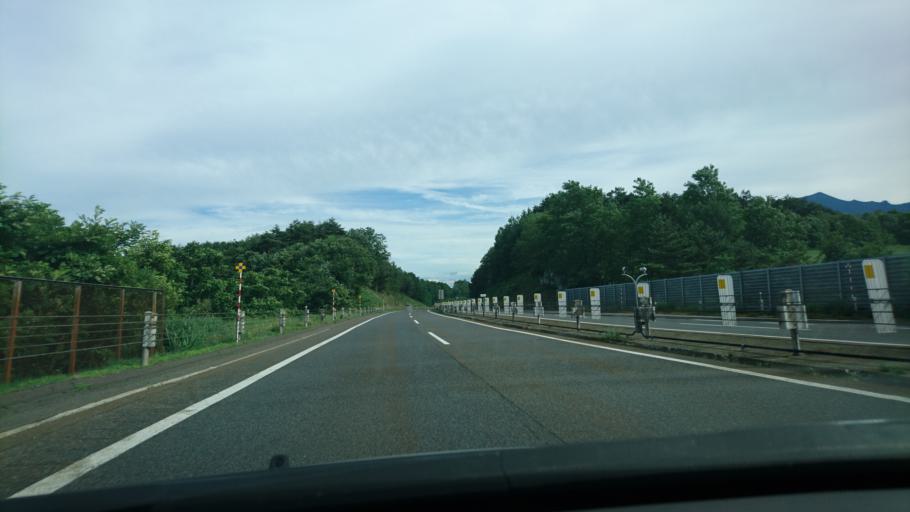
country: JP
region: Iwate
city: Shizukuishi
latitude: 39.9664
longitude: 141.0293
